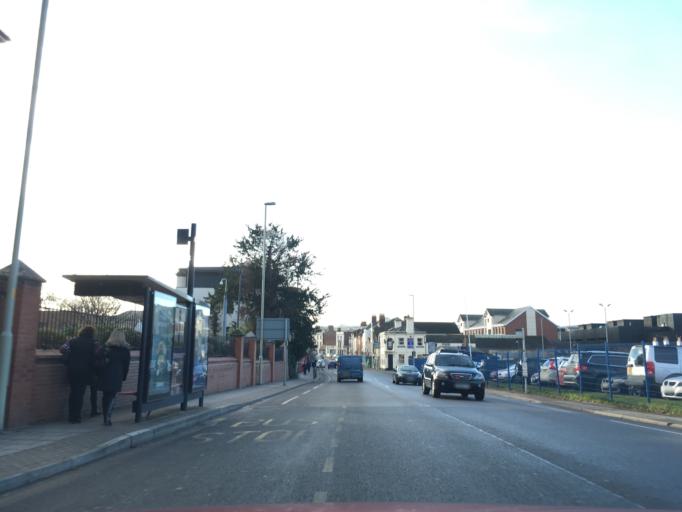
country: GB
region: England
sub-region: Gloucestershire
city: Gloucester
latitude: 51.8626
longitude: -2.2494
